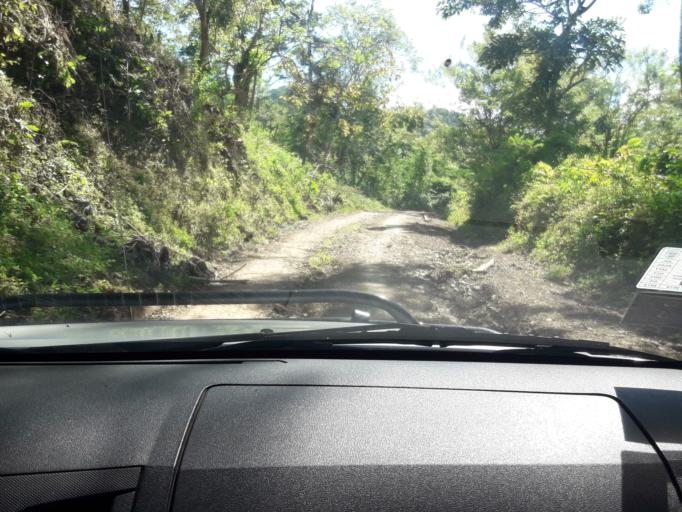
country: CR
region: Guanacaste
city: La Cruz
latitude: 11.2046
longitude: -85.6533
